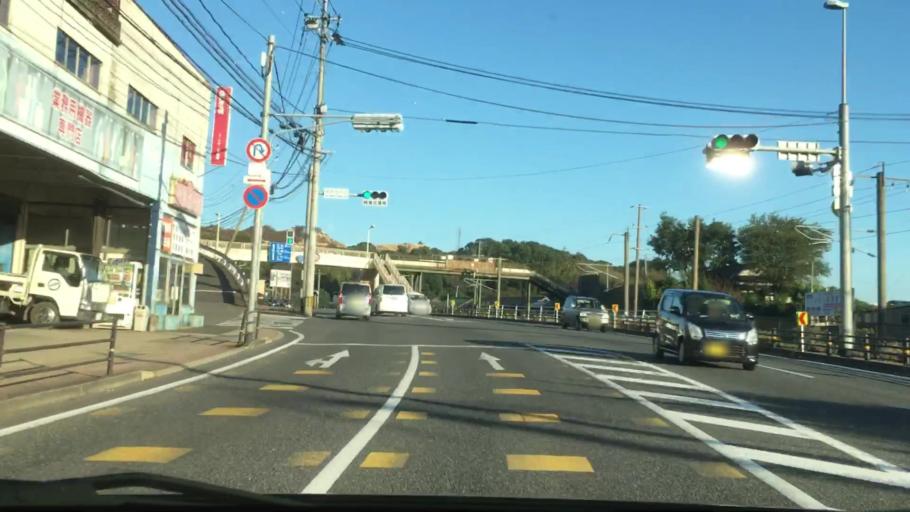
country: JP
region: Nagasaki
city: Sasebo
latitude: 33.1563
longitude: 129.7533
